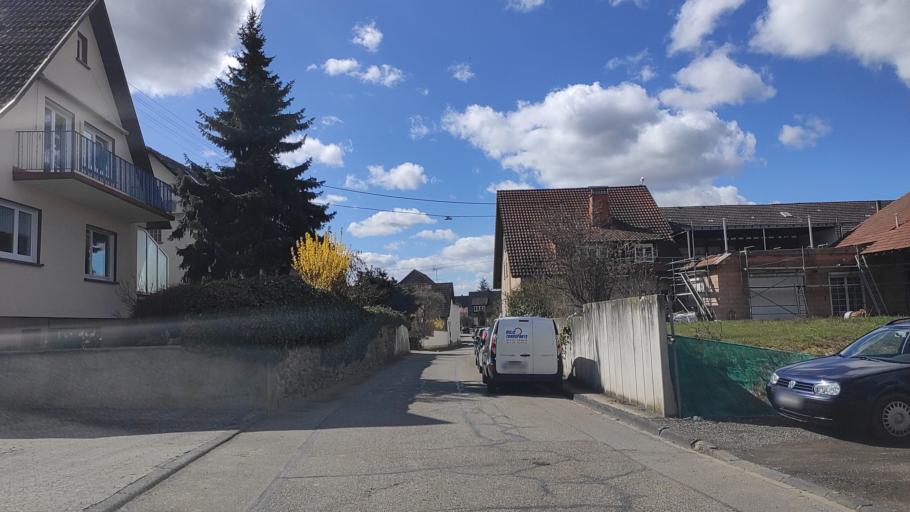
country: DE
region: Baden-Wuerttemberg
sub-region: Freiburg Region
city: Heitersheim
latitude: 47.8842
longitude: 7.6833
